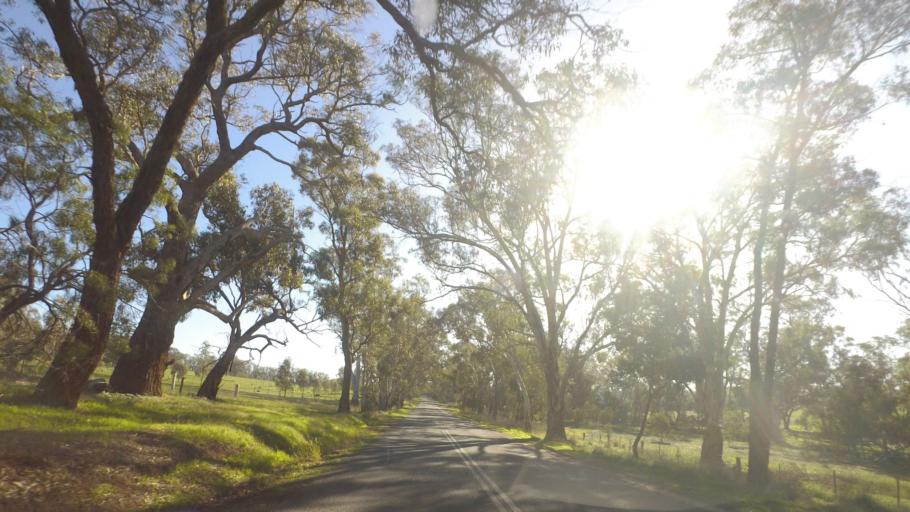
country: AU
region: Victoria
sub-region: Mount Alexander
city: Castlemaine
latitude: -36.9591
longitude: 144.3495
